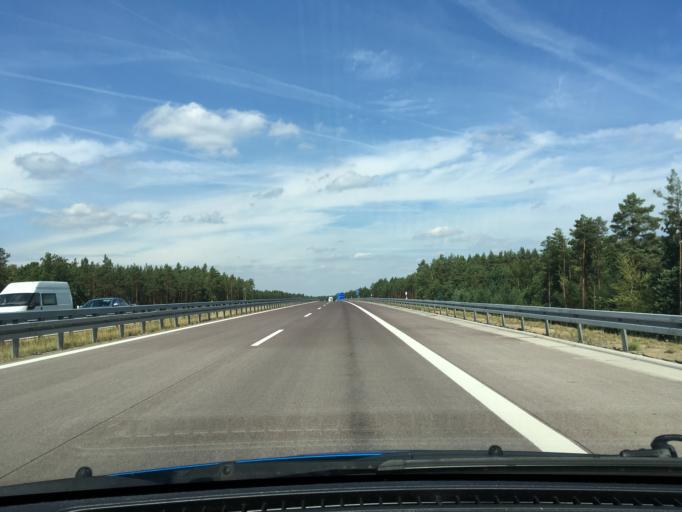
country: DE
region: Mecklenburg-Vorpommern
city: Gross Laasch
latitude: 53.3347
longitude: 11.5247
